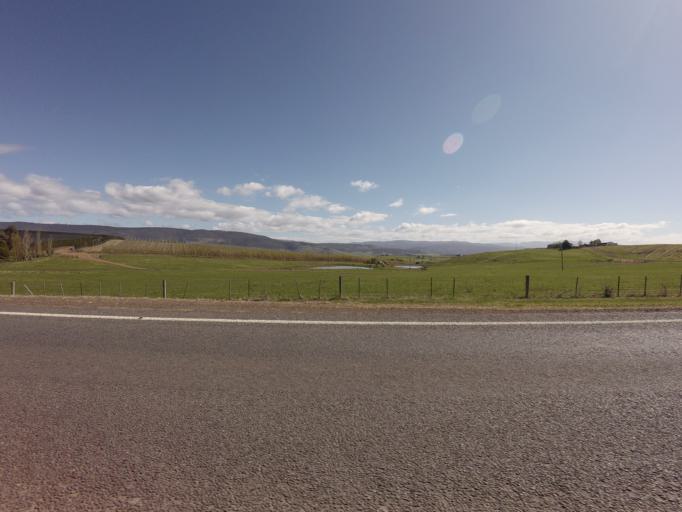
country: AU
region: Tasmania
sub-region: Derwent Valley
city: New Norfolk
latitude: -42.7066
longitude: 146.9443
